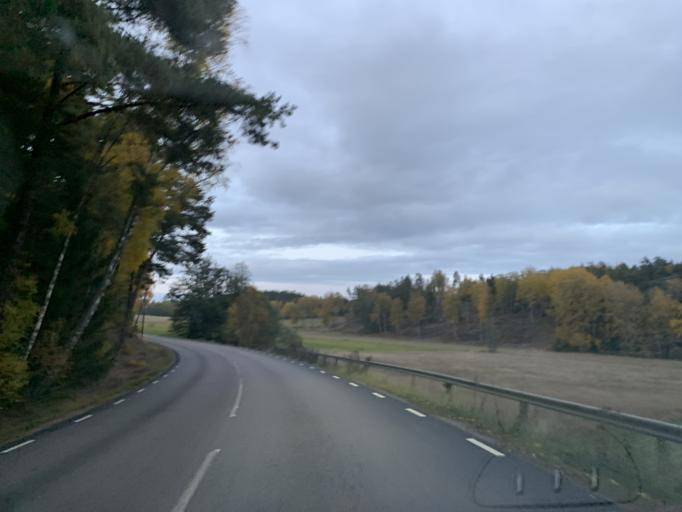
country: SE
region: Stockholm
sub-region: Nynashamns Kommun
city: Osmo
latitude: 58.9869
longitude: 17.7900
